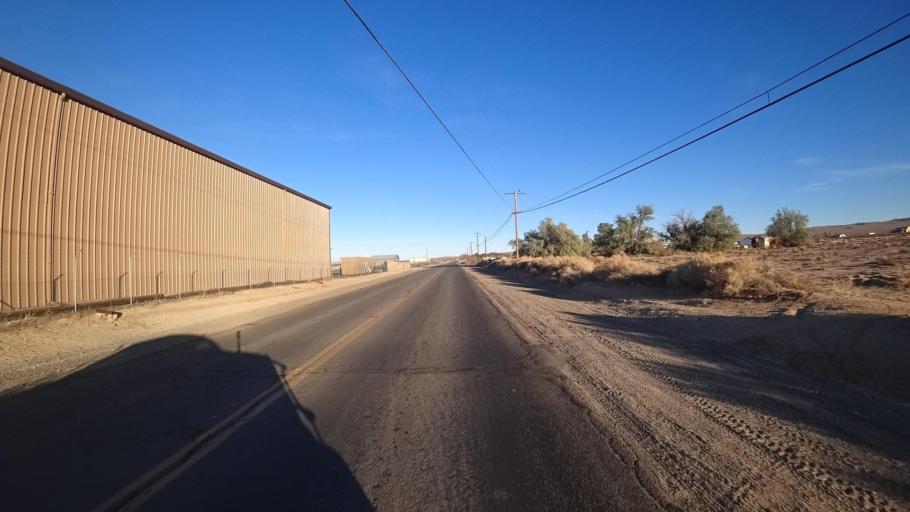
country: US
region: California
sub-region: Kern County
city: Ridgecrest
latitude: 35.6081
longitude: -117.6521
